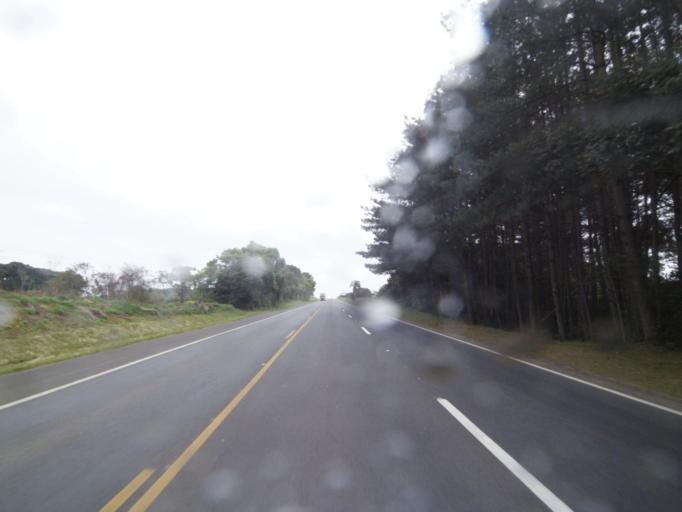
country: BR
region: Parana
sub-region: Palmeira
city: Palmeira
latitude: -25.4277
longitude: -50.1206
